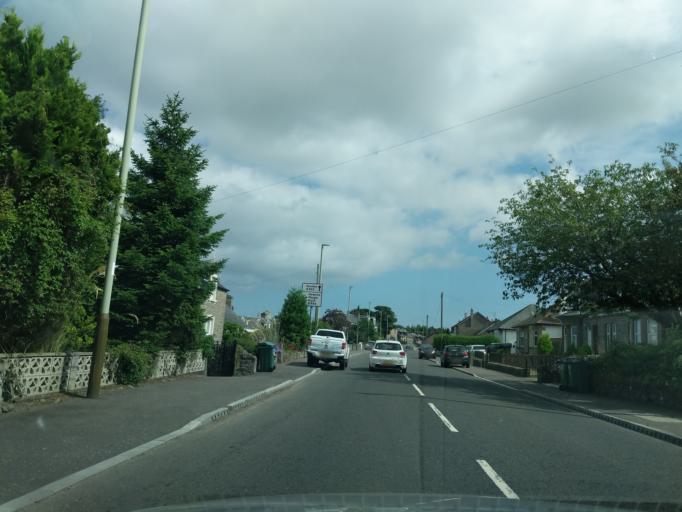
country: GB
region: Scotland
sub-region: Angus
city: Muirhead
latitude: 56.4977
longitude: -3.0706
